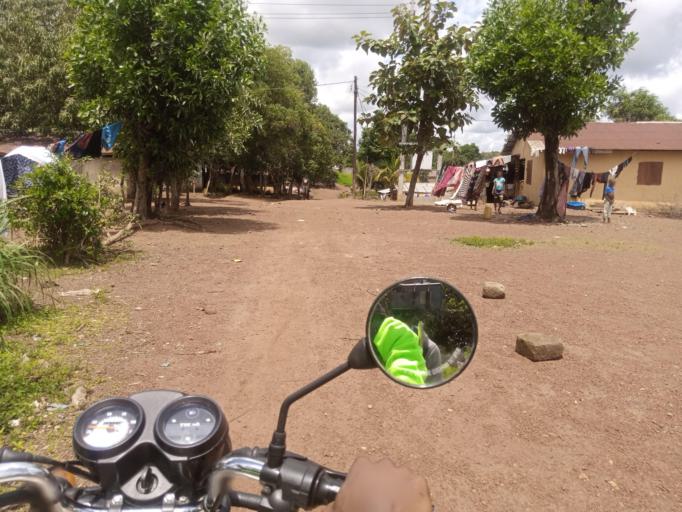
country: SL
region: Northern Province
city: Port Loko
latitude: 8.7595
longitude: -12.7812
